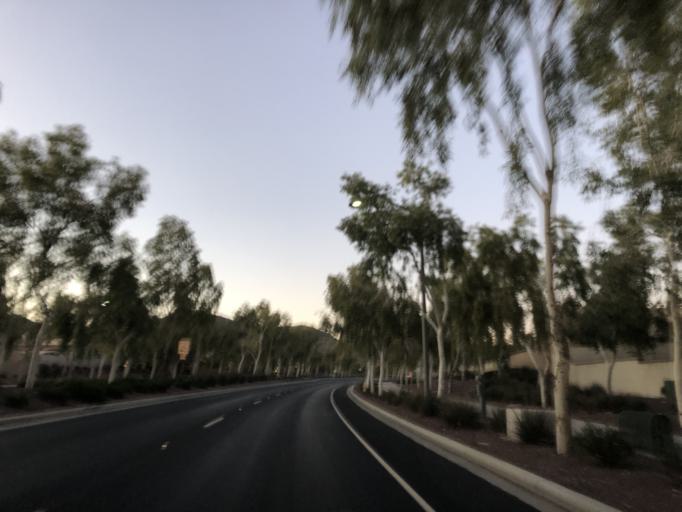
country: US
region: Arizona
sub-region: Maricopa County
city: Citrus Park
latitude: 33.4811
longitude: -112.5089
